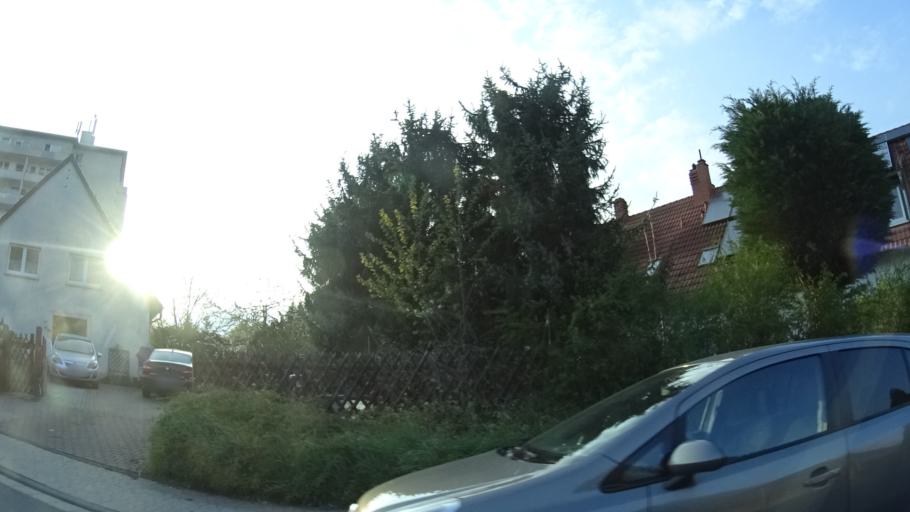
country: DE
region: Rheinland-Pfalz
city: Bad Kreuznach
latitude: 49.8453
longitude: 7.8458
